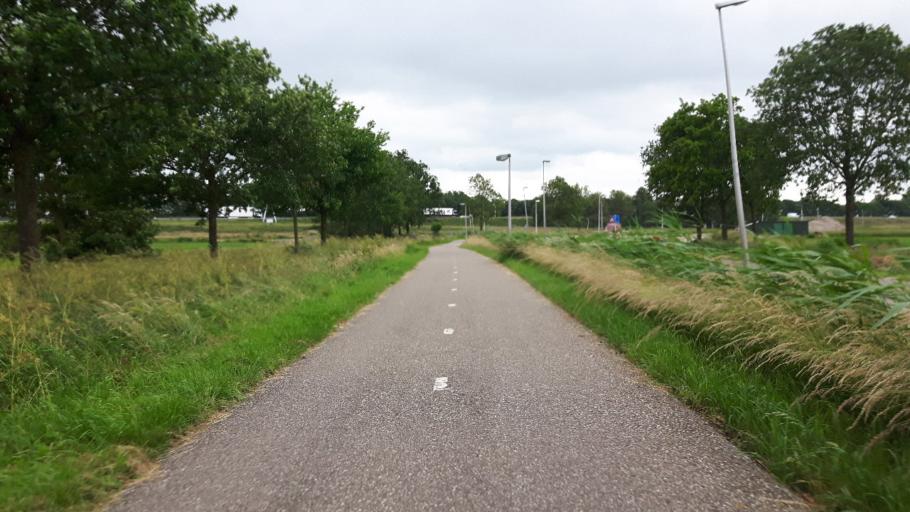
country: NL
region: Utrecht
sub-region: Gemeente Woerden
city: Woerden
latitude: 52.0690
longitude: 4.8246
